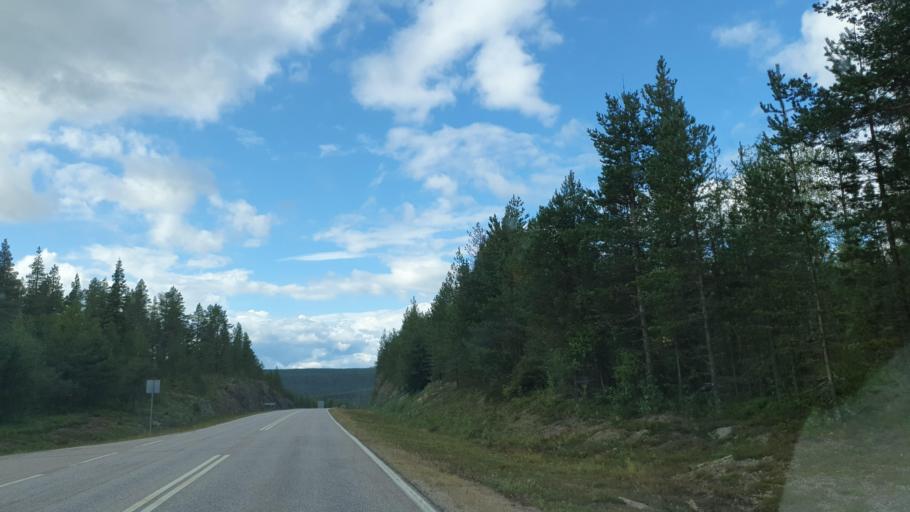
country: FI
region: Lapland
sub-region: Tunturi-Lappi
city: Muonio
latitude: 67.8610
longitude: 24.0981
